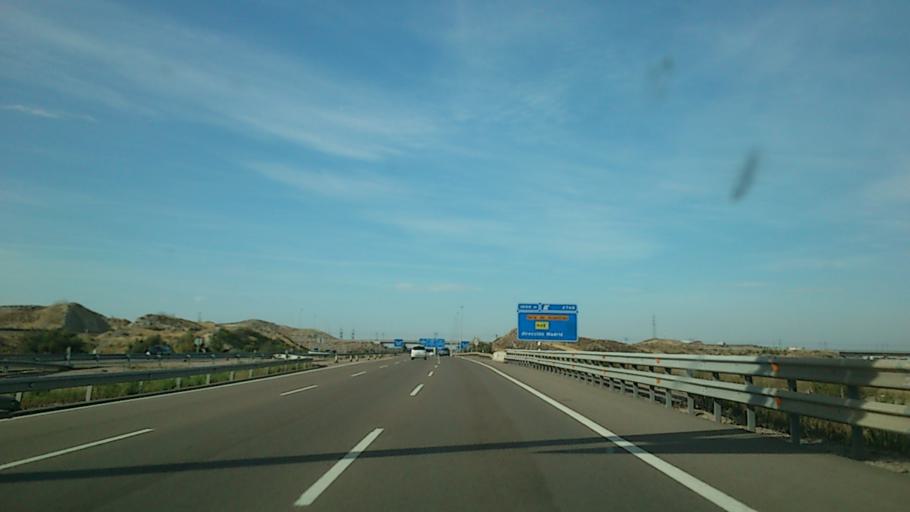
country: ES
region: Aragon
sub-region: Provincia de Zaragoza
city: Cuarte de Huerva
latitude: 41.6030
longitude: -0.9364
